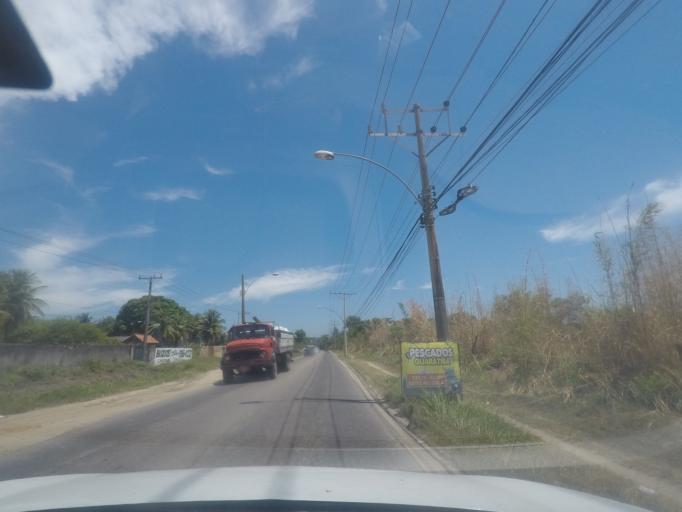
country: BR
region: Rio de Janeiro
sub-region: Itaguai
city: Itaguai
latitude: -22.9894
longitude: -43.6518
